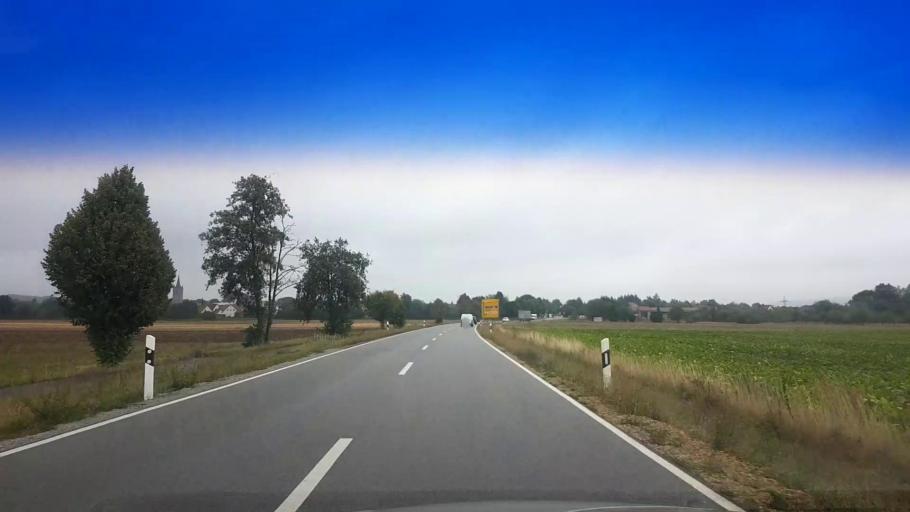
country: DE
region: Bavaria
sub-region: Upper Franconia
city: Eggolsheim
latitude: 49.7785
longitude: 11.0503
